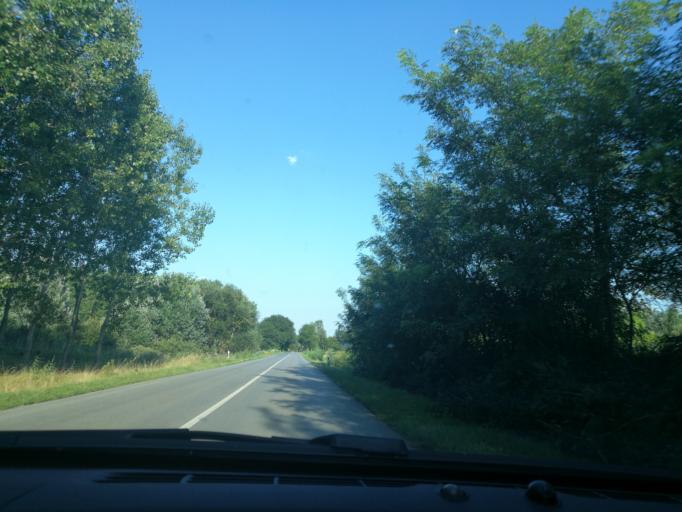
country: HU
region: Szabolcs-Szatmar-Bereg
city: Buj
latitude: 48.1203
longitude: 21.6491
